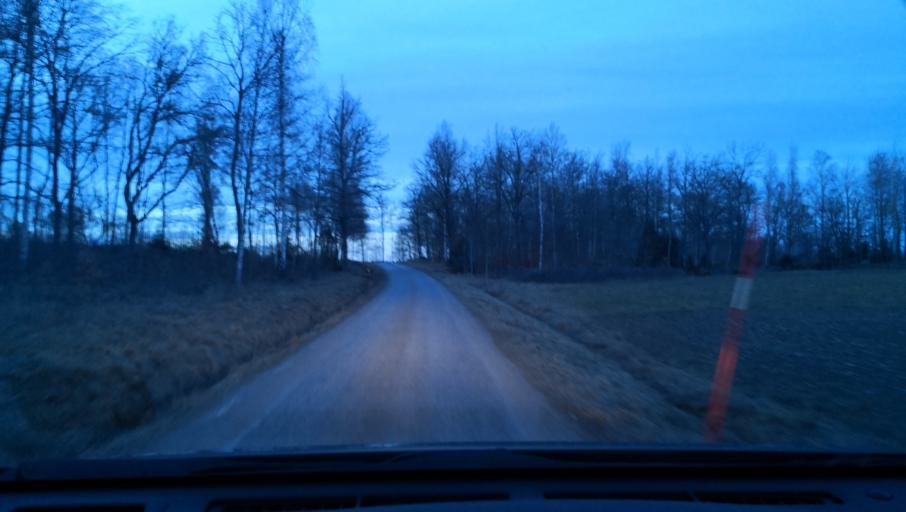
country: SE
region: Uppsala
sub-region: Enkopings Kommun
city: Dalby
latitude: 59.5508
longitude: 17.3685
